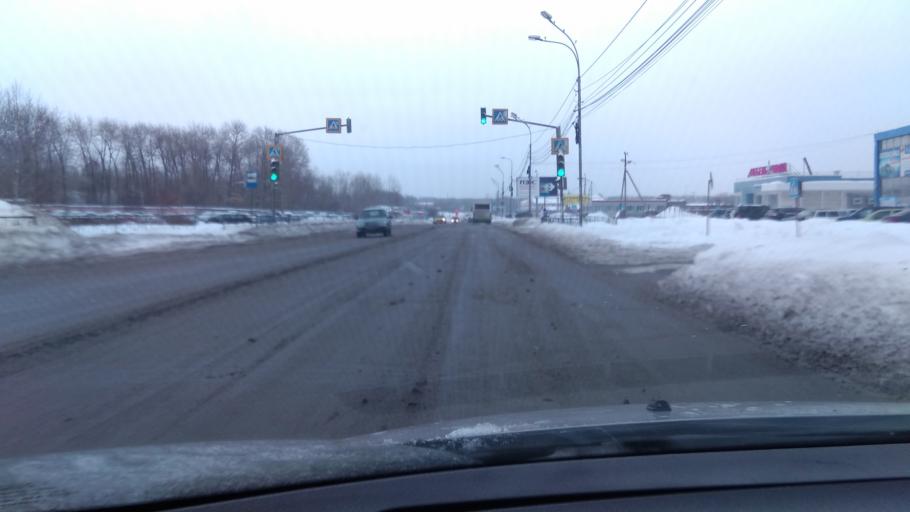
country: RU
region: Sverdlovsk
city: Nizhniy Tagil
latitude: 57.9090
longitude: 60.0215
